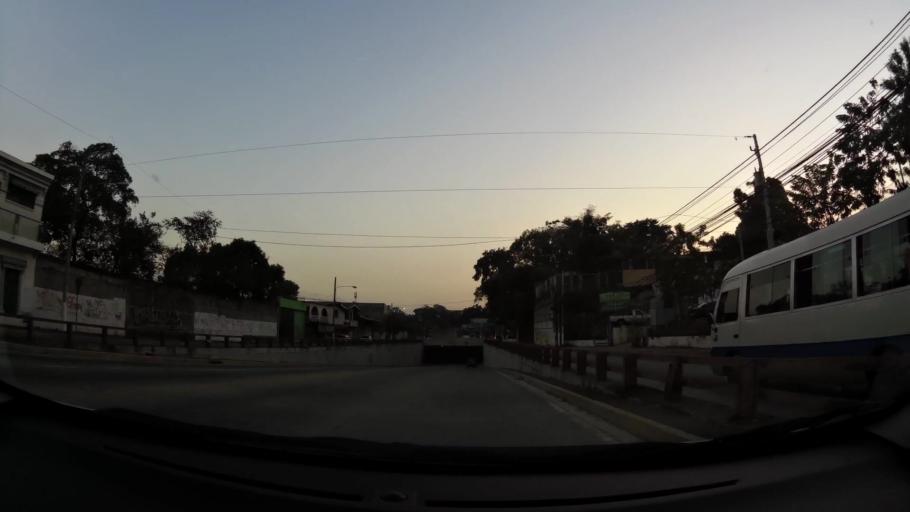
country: SV
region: San Salvador
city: Mejicanos
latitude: 13.7092
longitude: -89.2262
